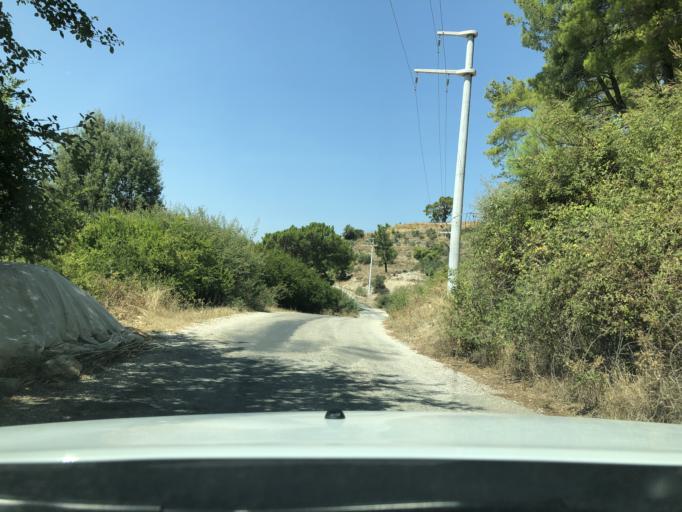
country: TR
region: Antalya
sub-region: Manavgat
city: Kizilagac
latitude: 36.8632
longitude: 31.5636
